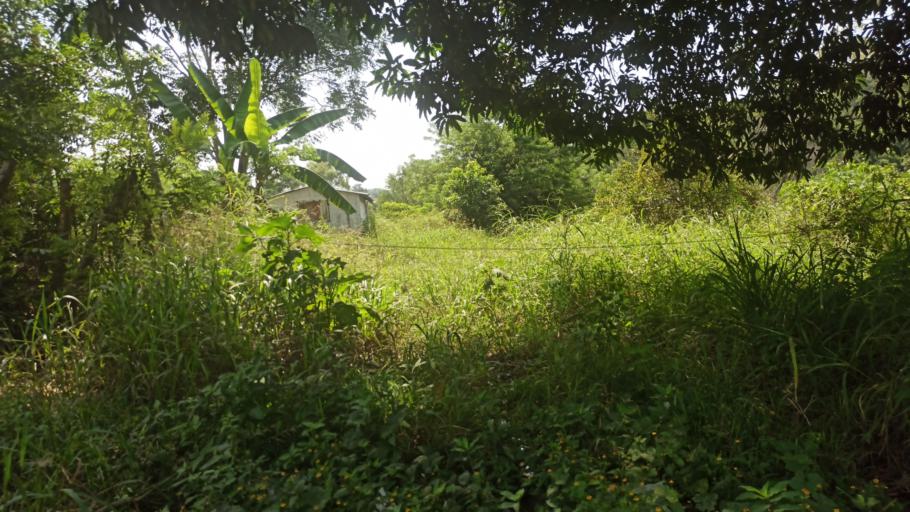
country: MX
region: Veracruz
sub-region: Atzalan
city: Colonias Pedernales
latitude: 20.0477
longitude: -97.0076
